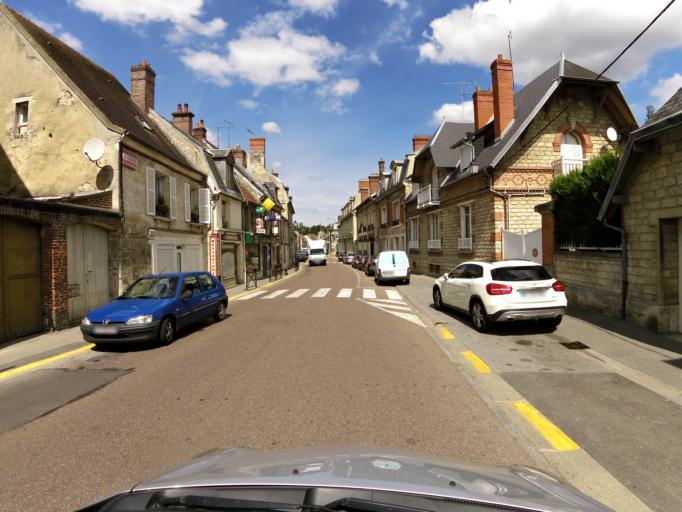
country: FR
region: Picardie
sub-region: Departement de l'Aisne
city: La Ferte-Milon
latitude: 49.1765
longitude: 3.1259
